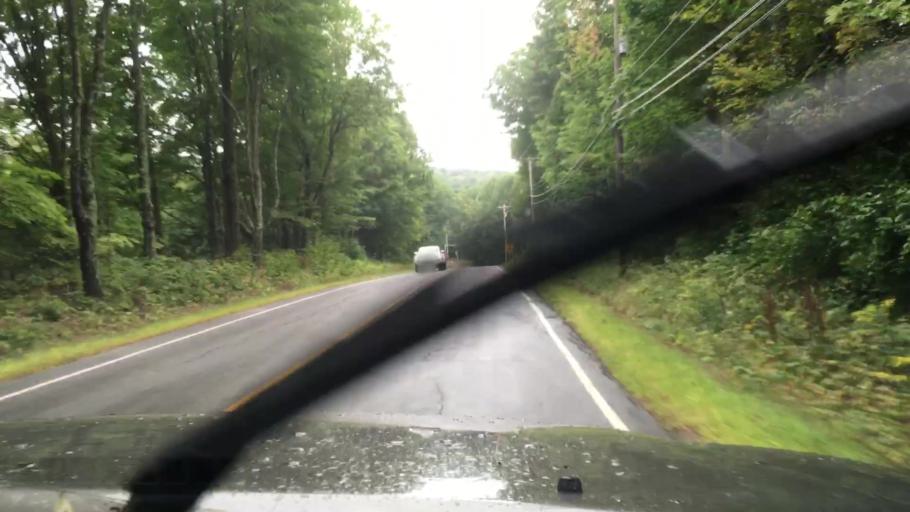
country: US
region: New Hampshire
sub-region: Belknap County
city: Meredith
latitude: 43.6411
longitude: -71.5323
